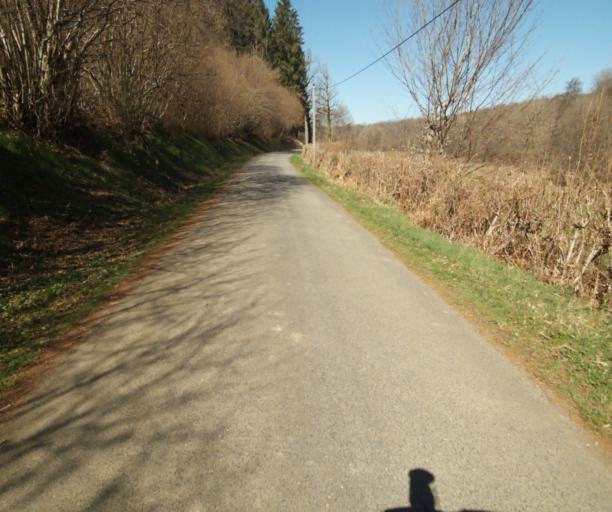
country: FR
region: Limousin
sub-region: Departement de la Correze
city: Saint-Clement
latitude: 45.3229
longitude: 1.7045
